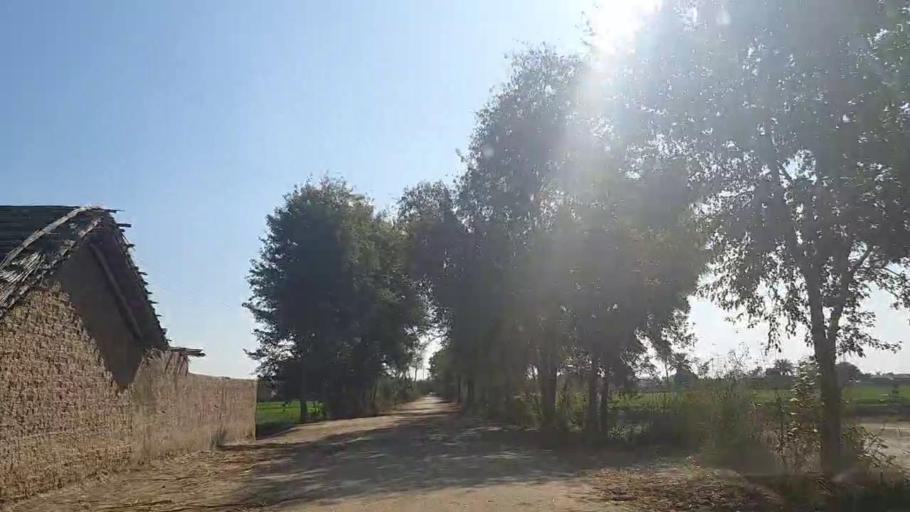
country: PK
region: Sindh
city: Sakrand
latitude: 26.2334
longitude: 68.1998
